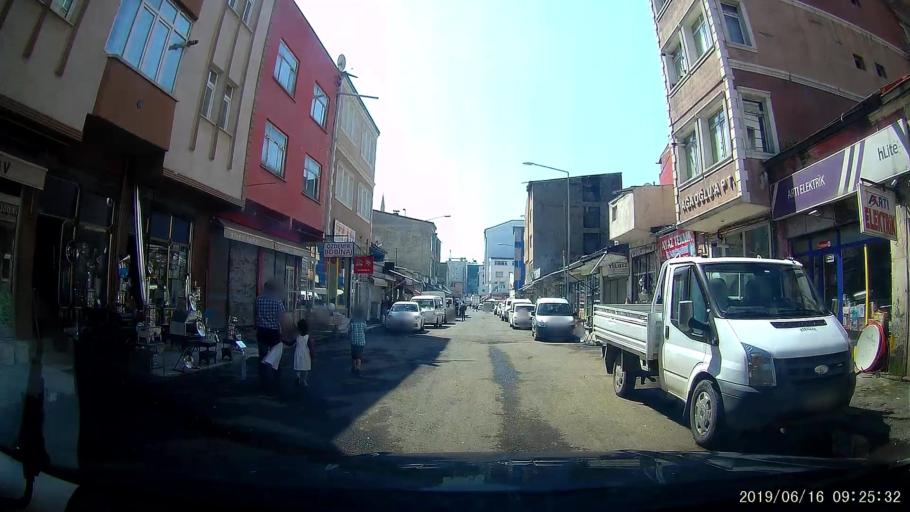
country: TR
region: Kars
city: Kars
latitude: 40.6089
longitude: 43.0958
